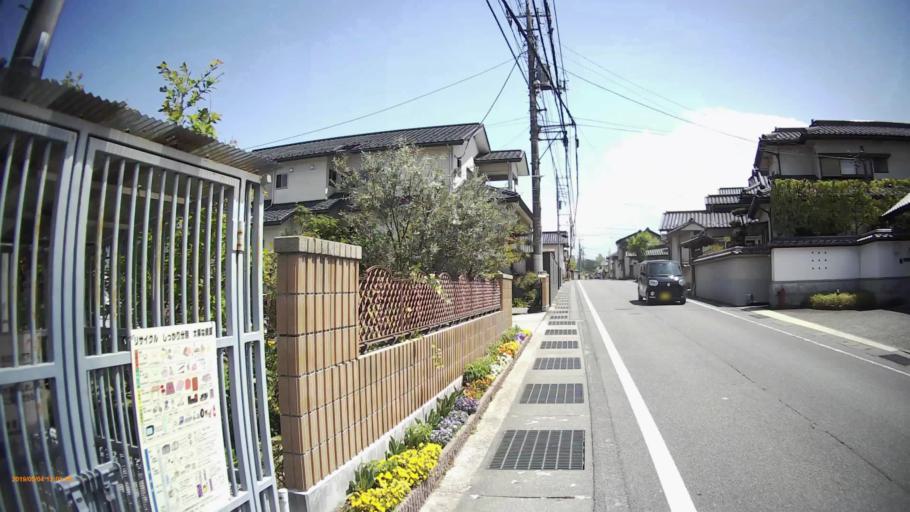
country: JP
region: Yamanashi
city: Ryuo
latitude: 35.6833
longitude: 138.4954
